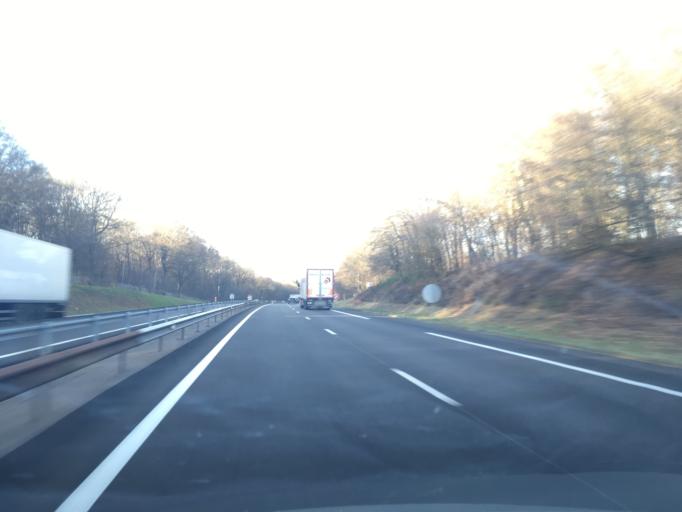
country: FR
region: Bourgogne
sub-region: Departement de l'Yonne
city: Joux-la-Ville
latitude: 47.5890
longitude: 3.9181
